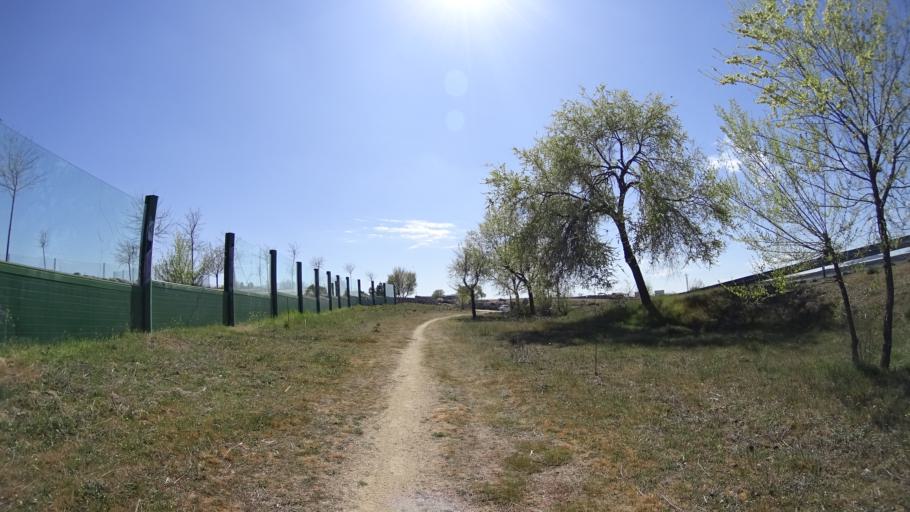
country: ES
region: Madrid
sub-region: Provincia de Madrid
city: Colmenar Viejo
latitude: 40.6494
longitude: -3.7925
